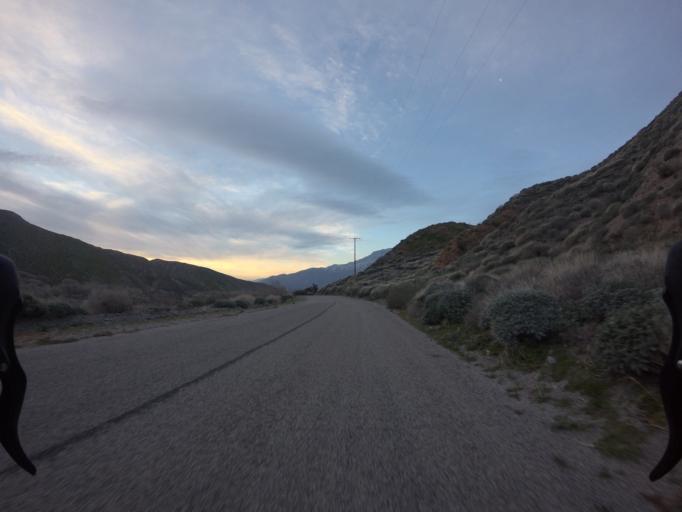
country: US
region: California
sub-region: Riverside County
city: Garnet
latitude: 33.9542
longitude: -116.6450
